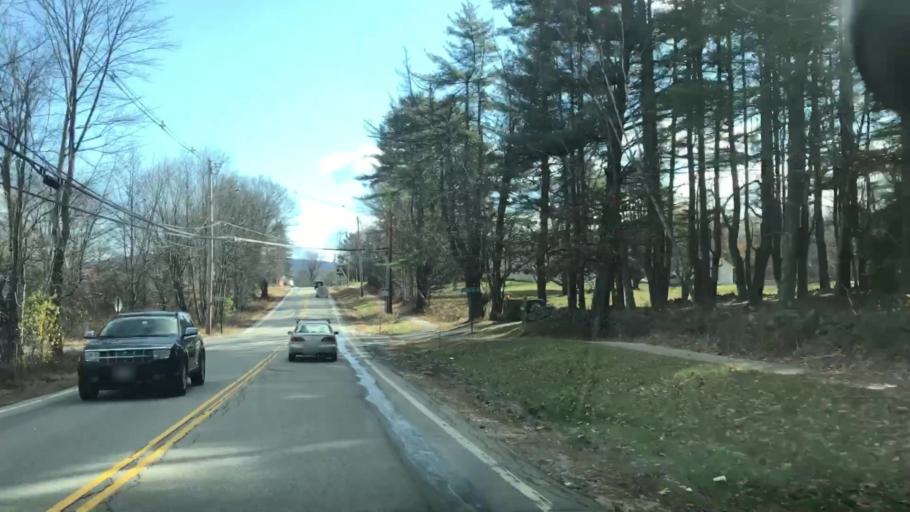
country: US
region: New Hampshire
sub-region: Carroll County
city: Wolfeboro
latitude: 43.5708
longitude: -71.1833
